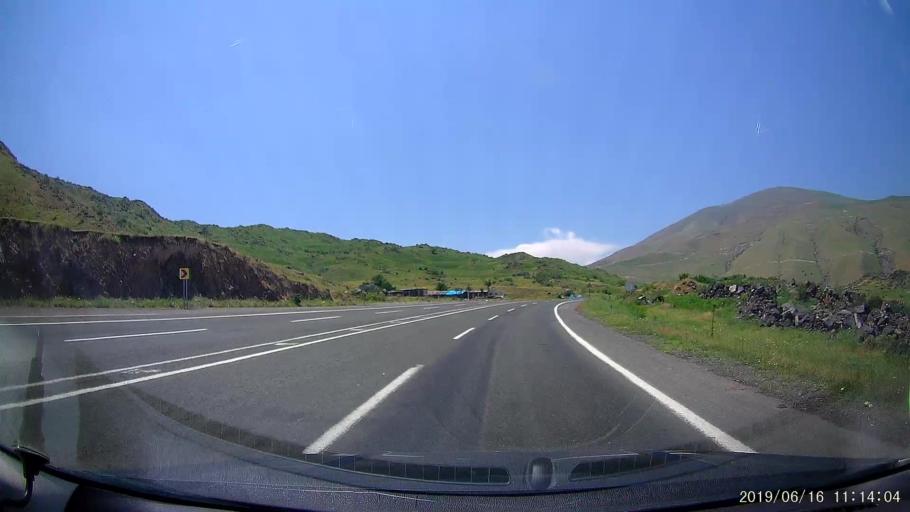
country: TR
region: Igdir
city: Igdir
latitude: 39.7838
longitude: 44.1459
